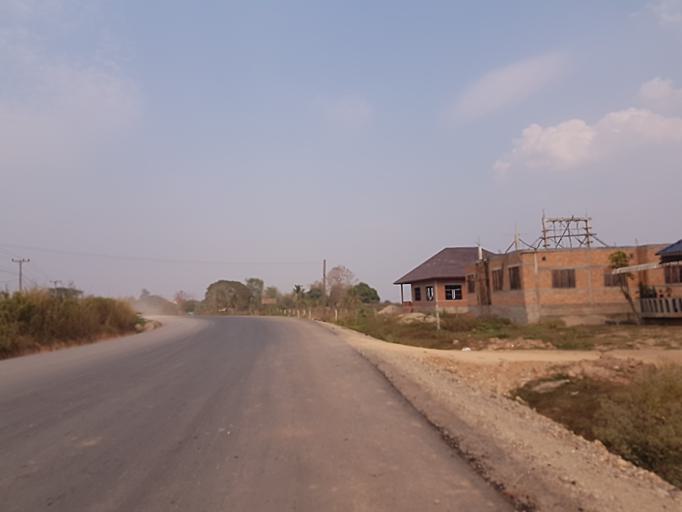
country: TH
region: Nong Khai
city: Nong Khai
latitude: 17.9720
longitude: 102.8487
